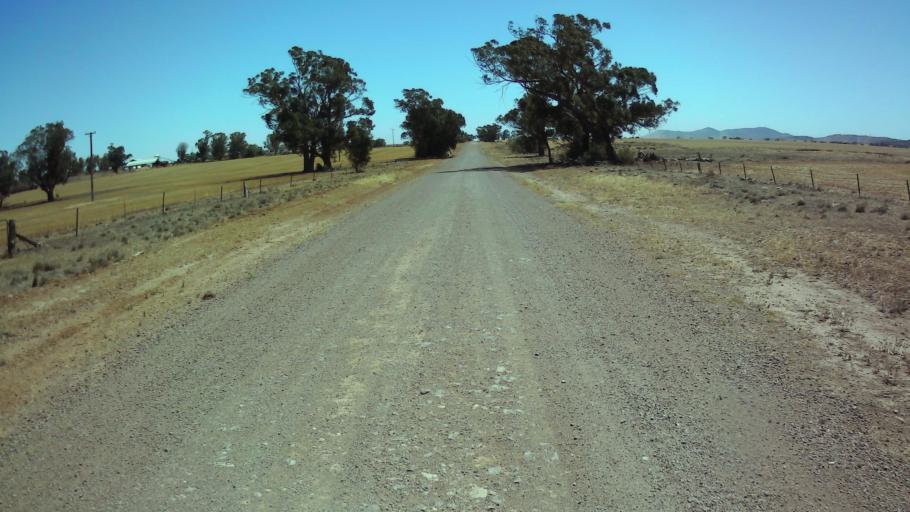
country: AU
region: New South Wales
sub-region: Forbes
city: Forbes
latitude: -33.7000
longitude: 147.7068
